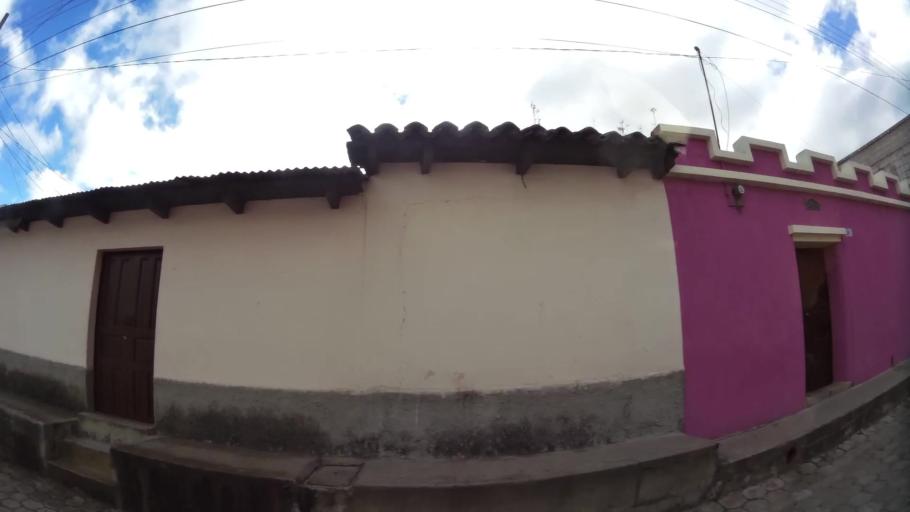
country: GT
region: Quetzaltenango
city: Salcaja
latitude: 14.8797
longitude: -91.4548
